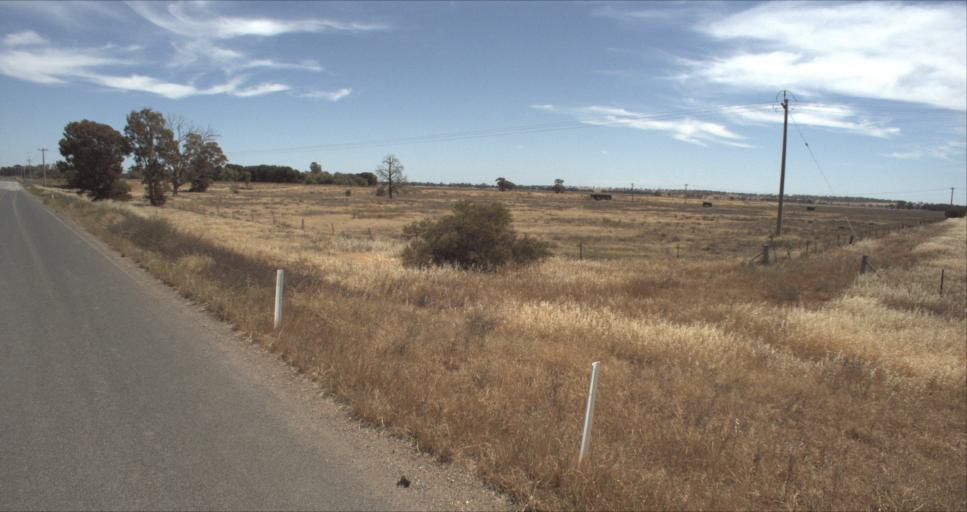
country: AU
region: New South Wales
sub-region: Leeton
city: Leeton
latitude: -34.6473
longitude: 146.4720
